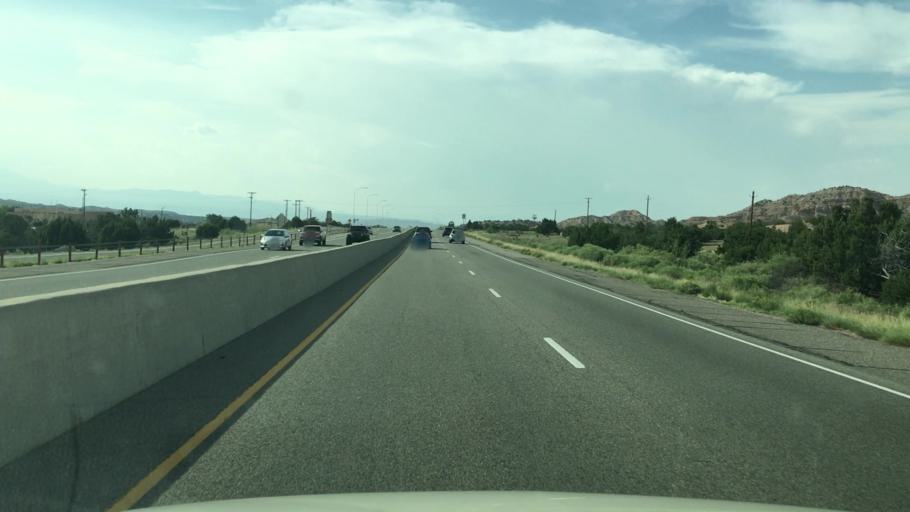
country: US
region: New Mexico
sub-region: Santa Fe County
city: Nambe
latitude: 35.8152
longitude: -105.9704
